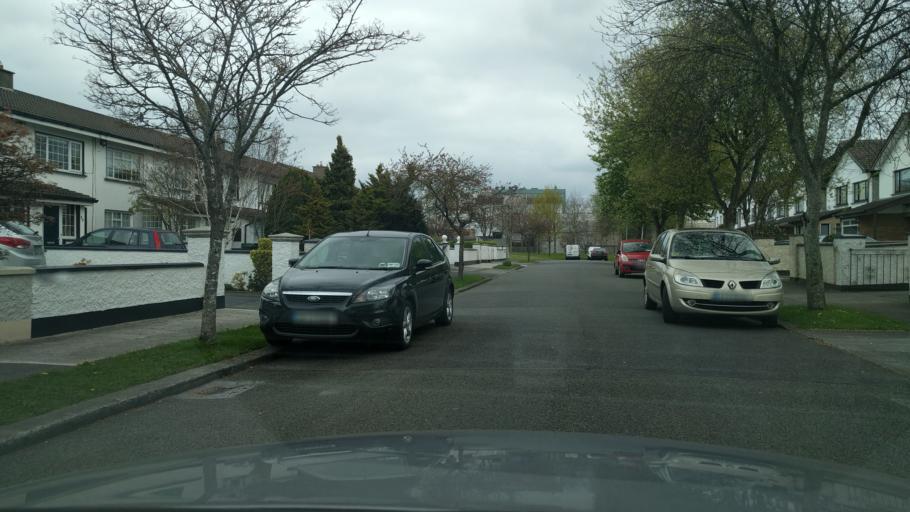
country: IE
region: Leinster
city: Clondalkin
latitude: 53.3148
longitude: -6.3866
